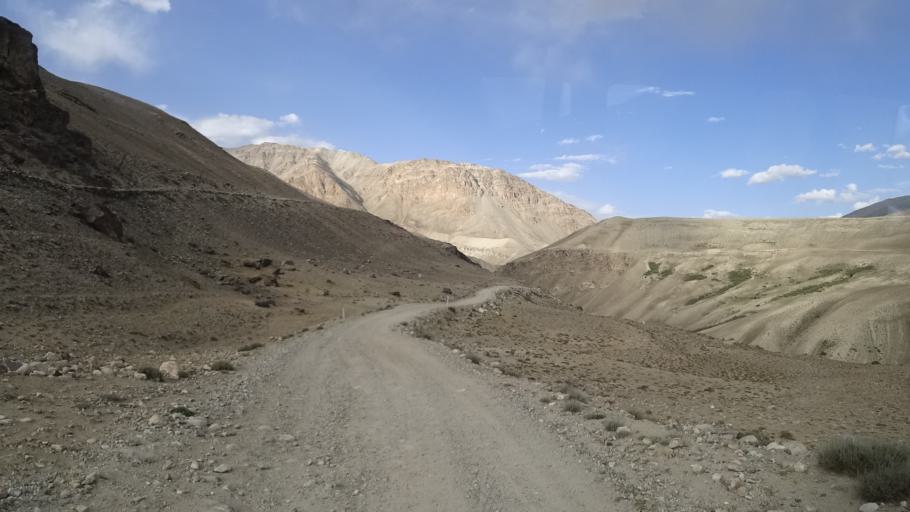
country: AF
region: Badakhshan
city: Khandud
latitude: 37.2257
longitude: 72.8033
